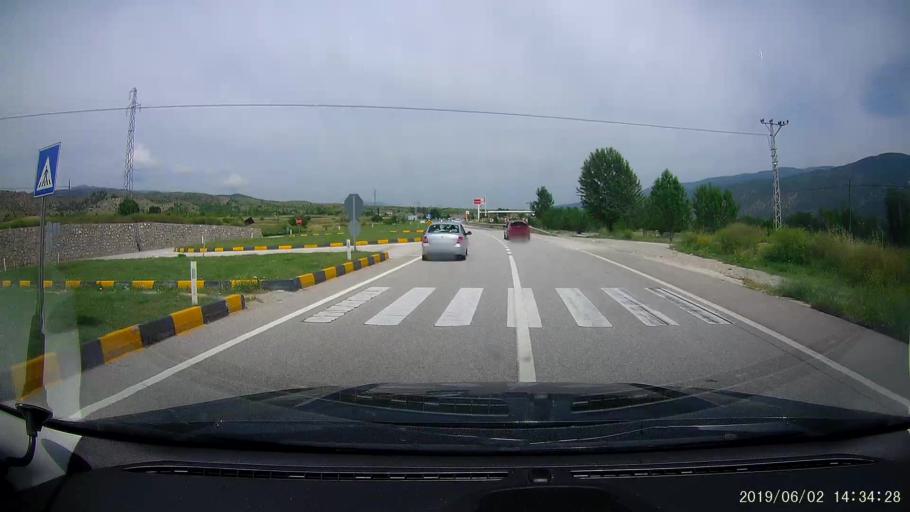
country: TR
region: Kastamonu
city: Tosya
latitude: 41.0382
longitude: 34.1936
